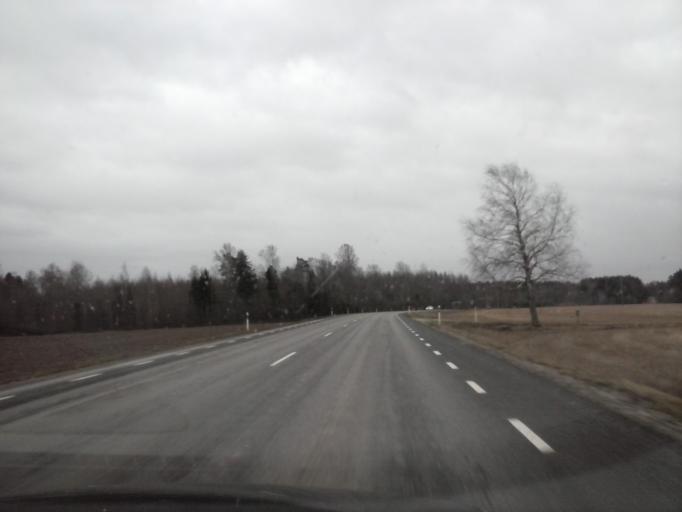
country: EE
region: Tartu
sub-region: UElenurme vald
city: Ulenurme
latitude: 58.1887
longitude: 26.8234
